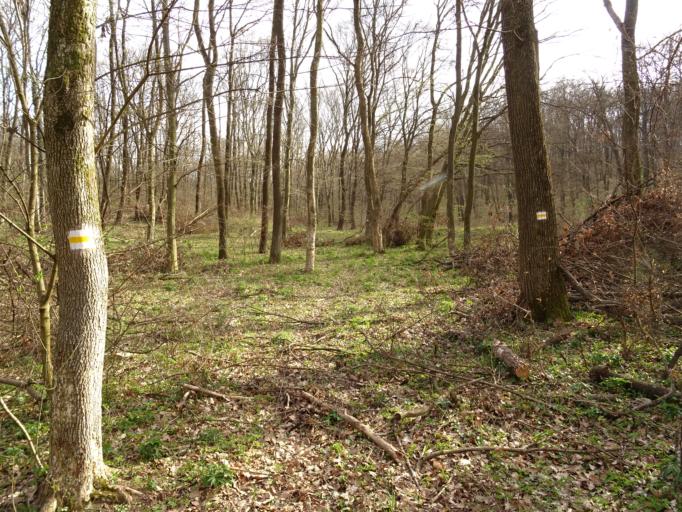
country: HU
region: Fejer
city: Pazmand
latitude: 47.2709
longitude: 18.5971
